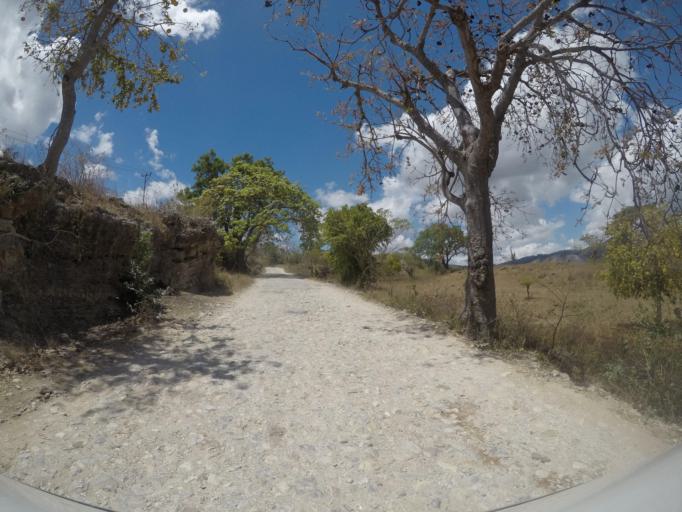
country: TL
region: Baucau
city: Baucau
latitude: -8.4840
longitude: 126.6252
